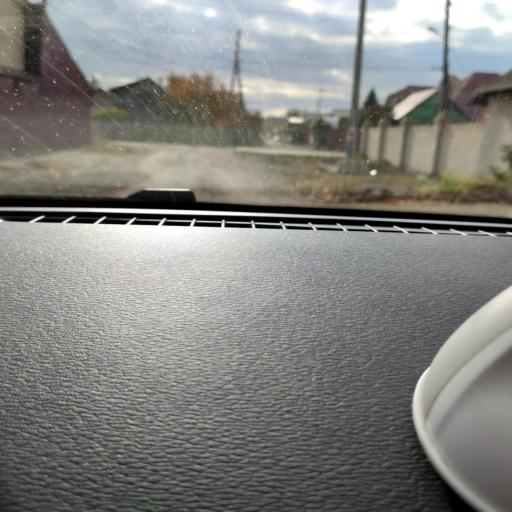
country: RU
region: Samara
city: Petra-Dubrava
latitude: 53.2524
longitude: 50.3116
